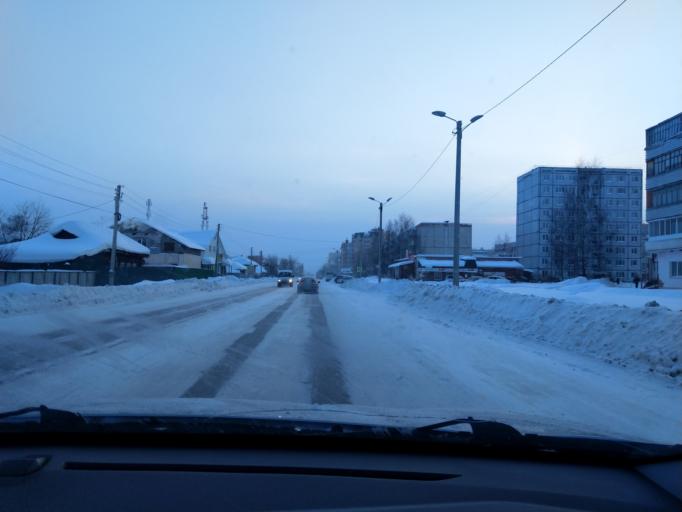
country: RU
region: Perm
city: Dobryanka
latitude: 58.4705
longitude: 56.4062
